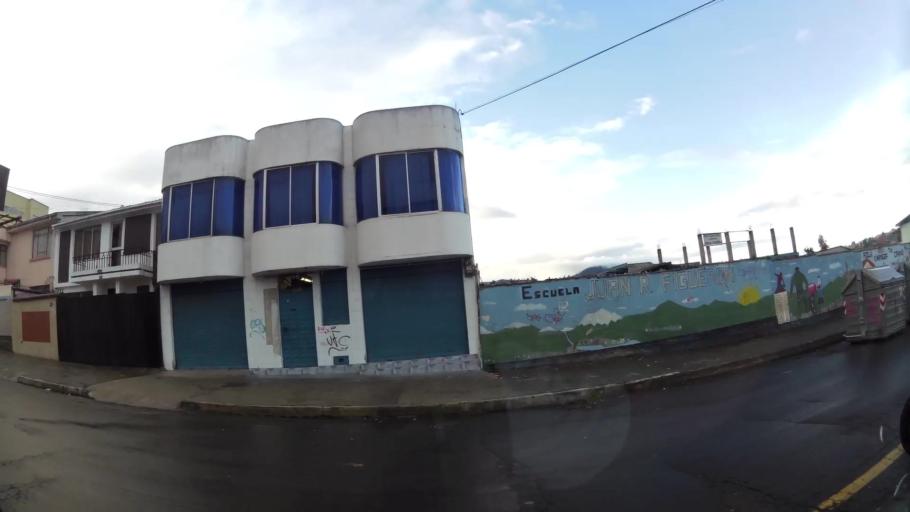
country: EC
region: Pichincha
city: Quito
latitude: -0.1137
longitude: -78.4924
